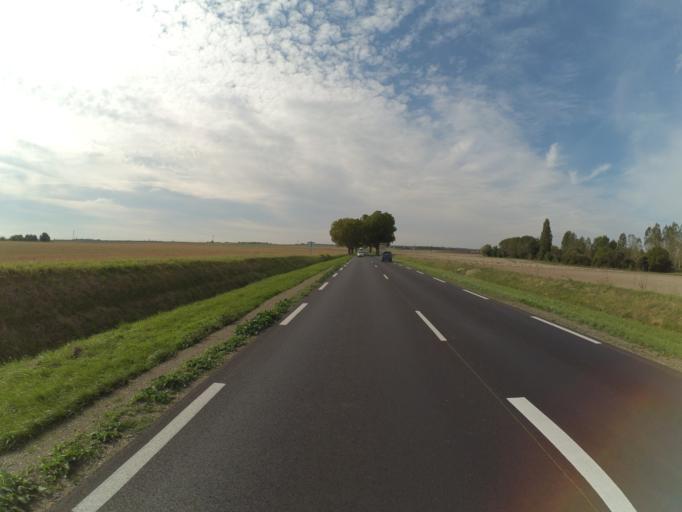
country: FR
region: Pays de la Loire
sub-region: Departement de Maine-et-Loire
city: Distre
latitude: 47.2233
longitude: -0.1479
